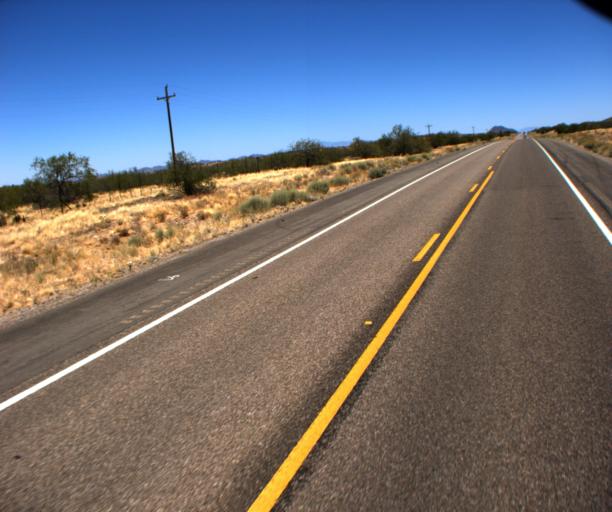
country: US
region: Arizona
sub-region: Pima County
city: Sells
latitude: 32.0203
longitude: -111.6108
